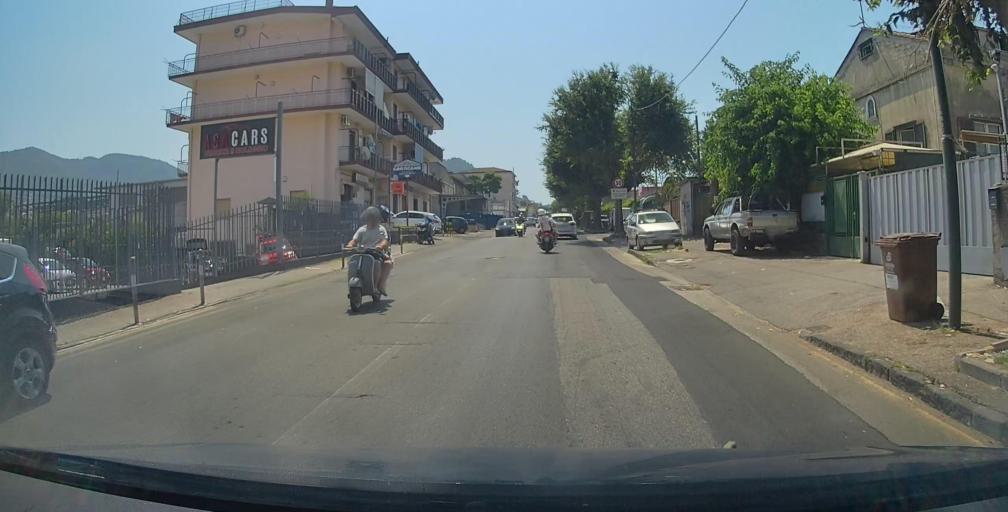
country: IT
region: Campania
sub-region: Provincia di Salerno
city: Cava De Tirreni
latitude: 40.7217
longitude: 14.6963
